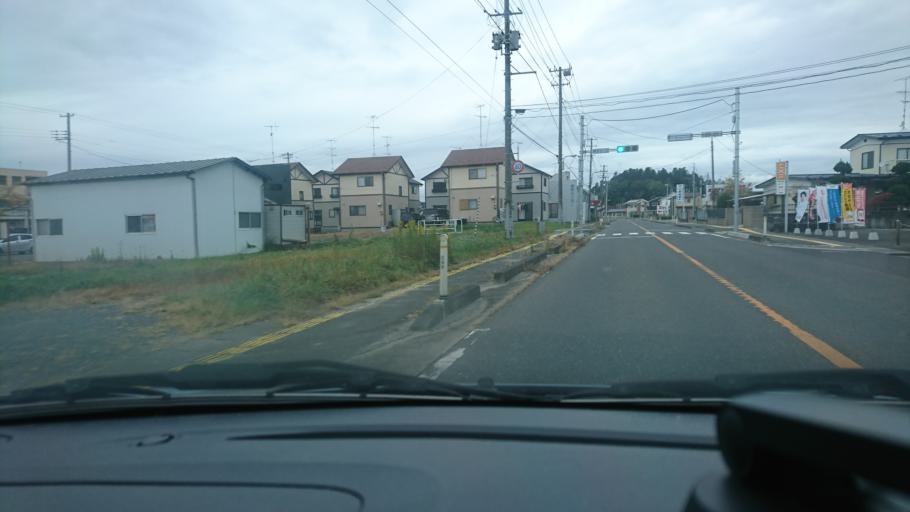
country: JP
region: Iwate
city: Ichinoseki
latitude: 38.7714
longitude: 141.1251
